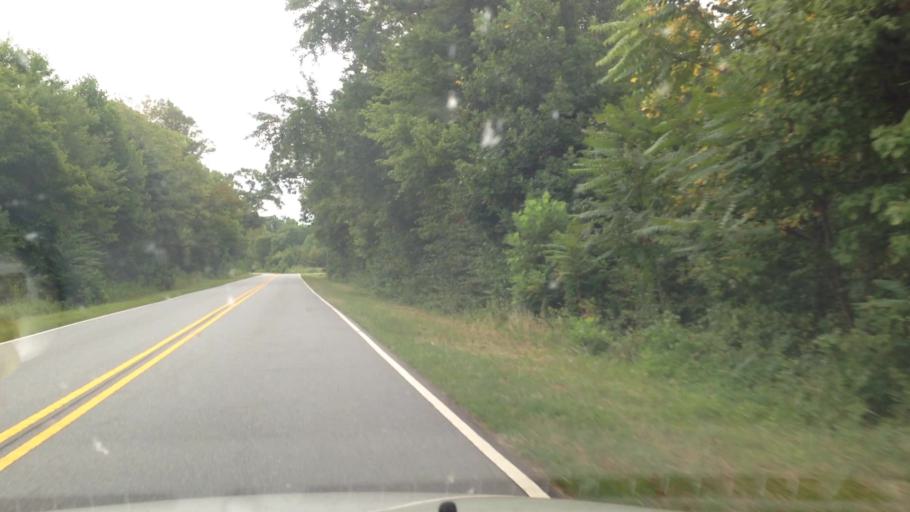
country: US
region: North Carolina
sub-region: Rockingham County
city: Mayodan
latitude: 36.4203
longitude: -80.0815
